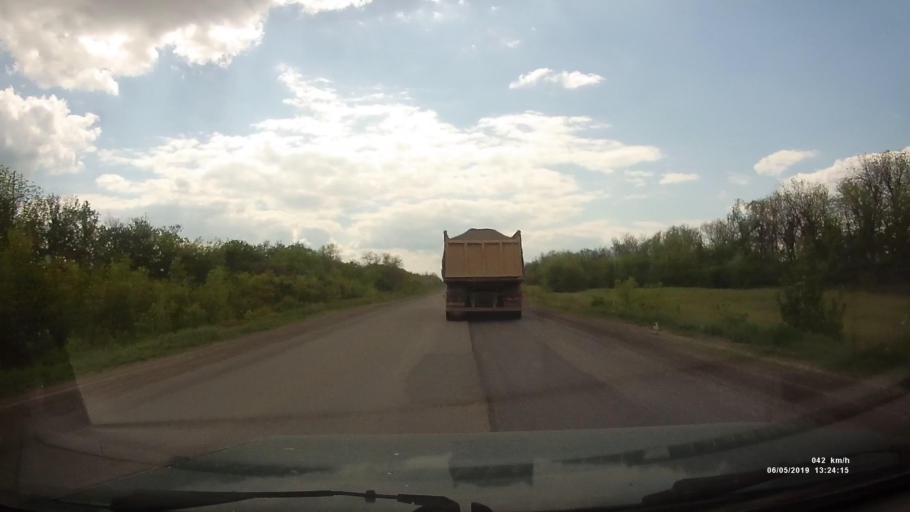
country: RU
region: Rostov
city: Ust'-Donetskiy
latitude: 47.6867
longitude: 40.9118
